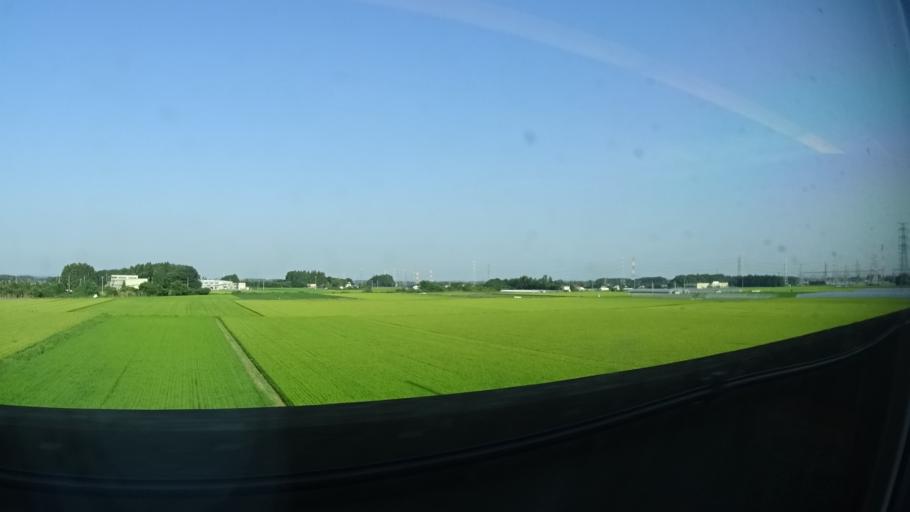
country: JP
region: Tochigi
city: Ujiie
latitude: 36.6696
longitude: 139.9153
